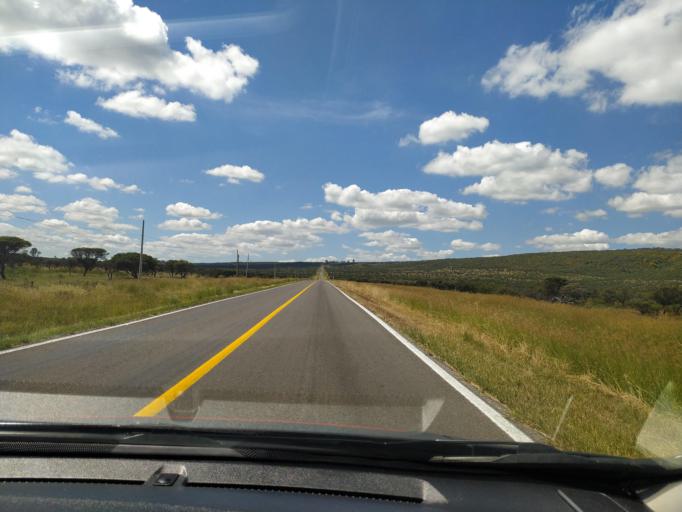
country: MX
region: Jalisco
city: San Miguel el Alto
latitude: 21.0171
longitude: -102.4929
